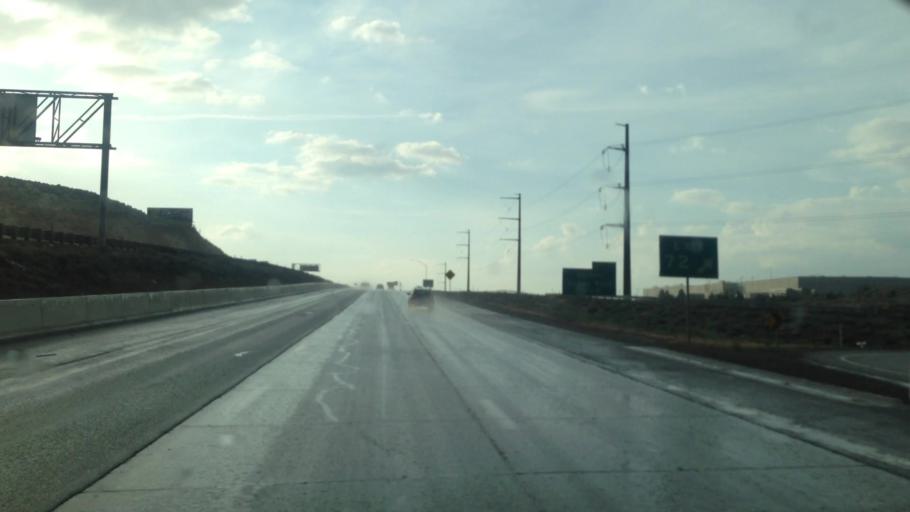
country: US
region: Nevada
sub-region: Washoe County
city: Golden Valley
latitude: 39.5910
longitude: -119.8275
